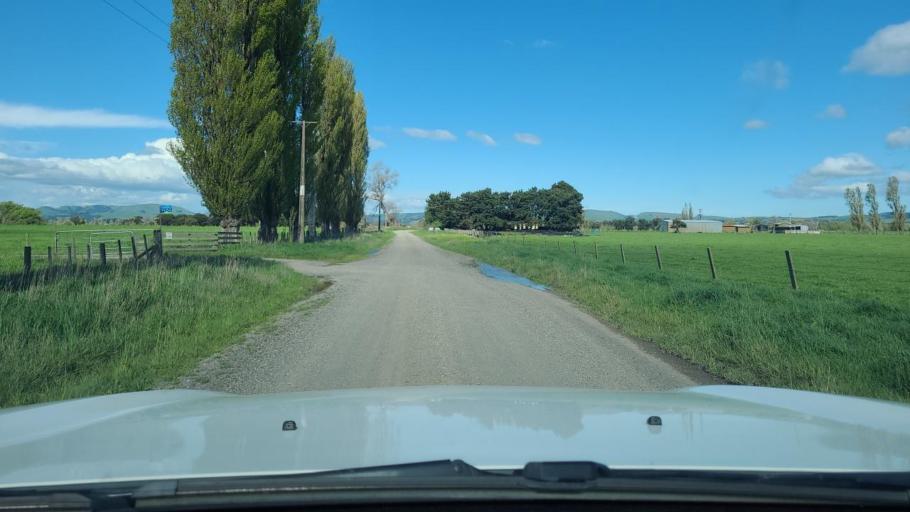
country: NZ
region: Wellington
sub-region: South Wairarapa District
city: Waipawa
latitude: -41.2103
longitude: 175.3922
